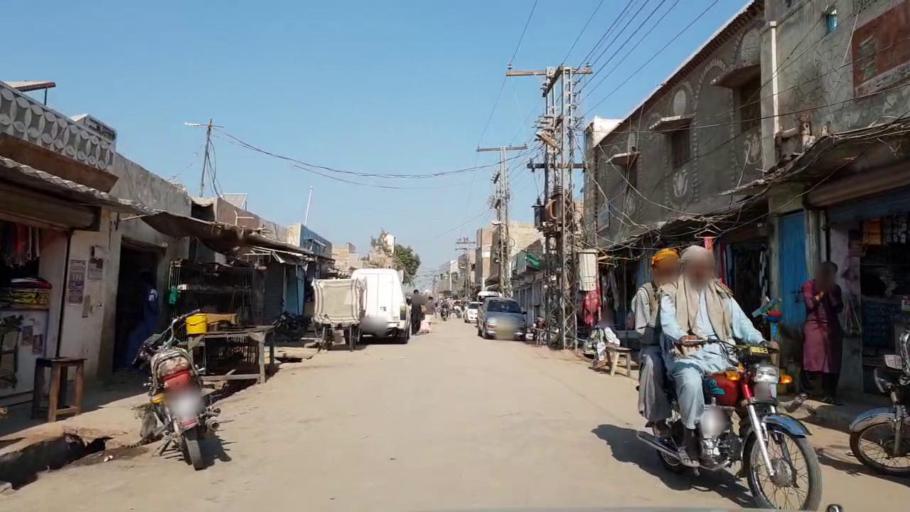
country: PK
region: Sindh
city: Tando Adam
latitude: 25.6330
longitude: 68.5946
